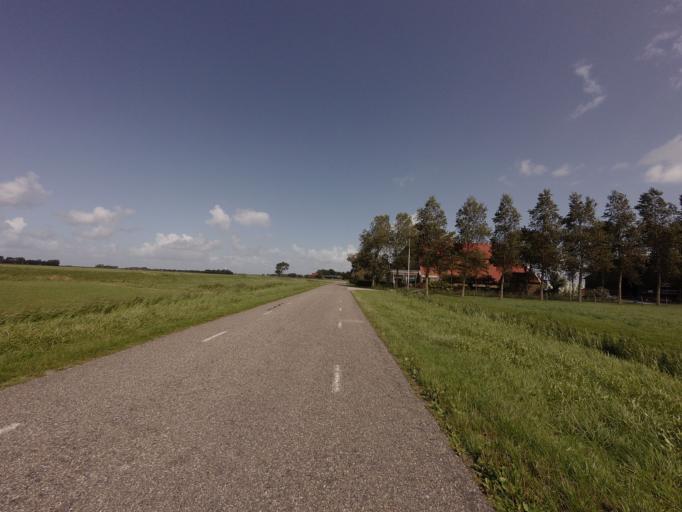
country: NL
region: Friesland
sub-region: Sudwest Fryslan
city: Makkum
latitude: 53.1045
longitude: 5.4312
